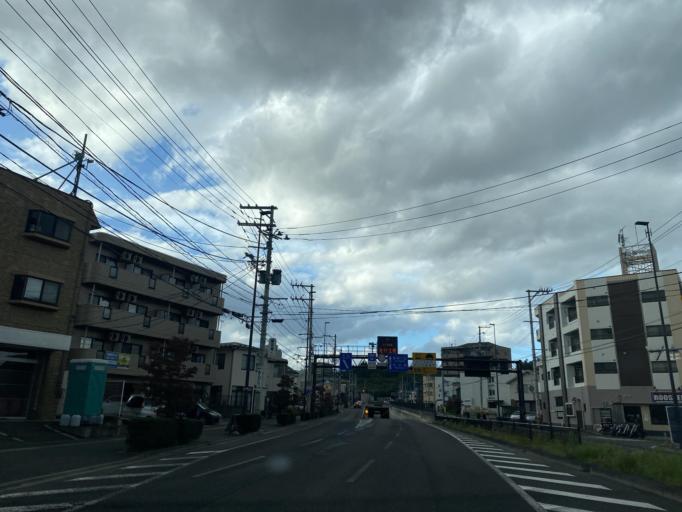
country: JP
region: Miyagi
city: Sendai-shi
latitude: 38.2786
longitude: 140.8603
